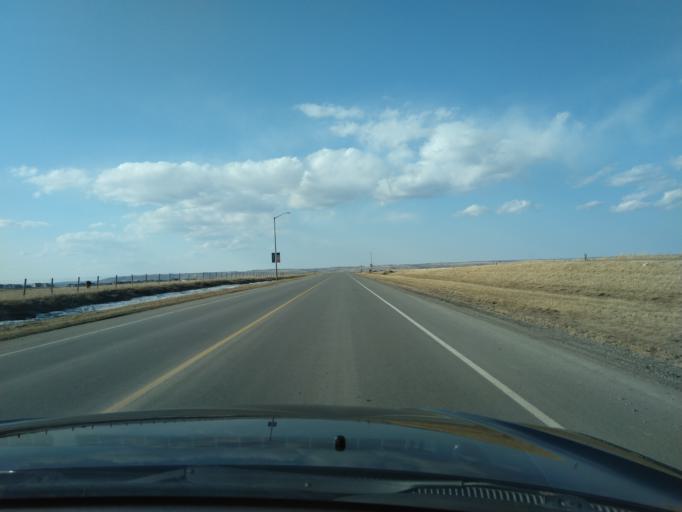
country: CA
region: Alberta
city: Cochrane
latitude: 51.0974
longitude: -114.3887
